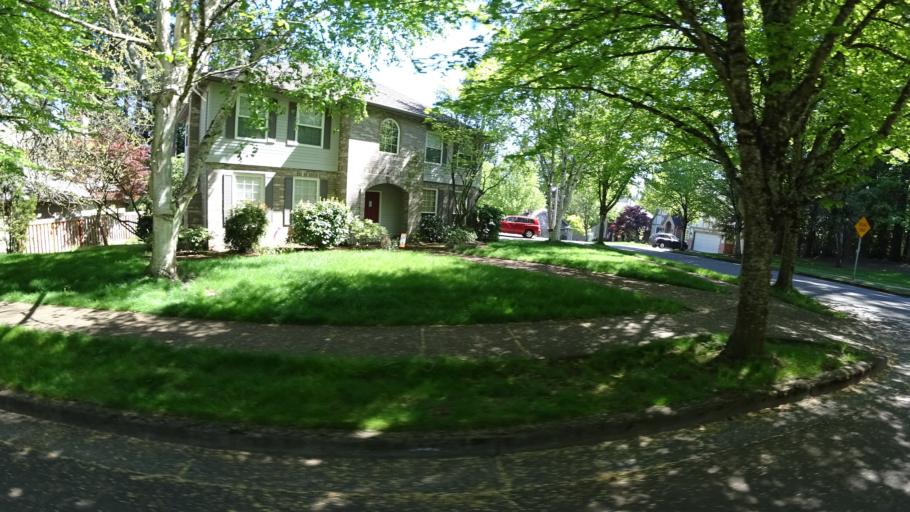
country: US
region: Oregon
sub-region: Washington County
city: Aloha
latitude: 45.4444
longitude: -122.8421
